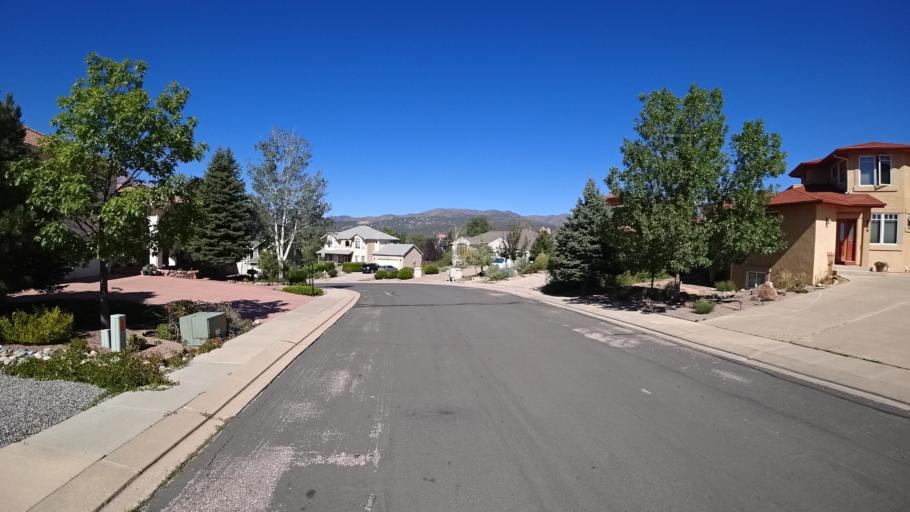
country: US
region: Colorado
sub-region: El Paso County
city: Colorado Springs
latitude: 38.8512
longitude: -104.8614
